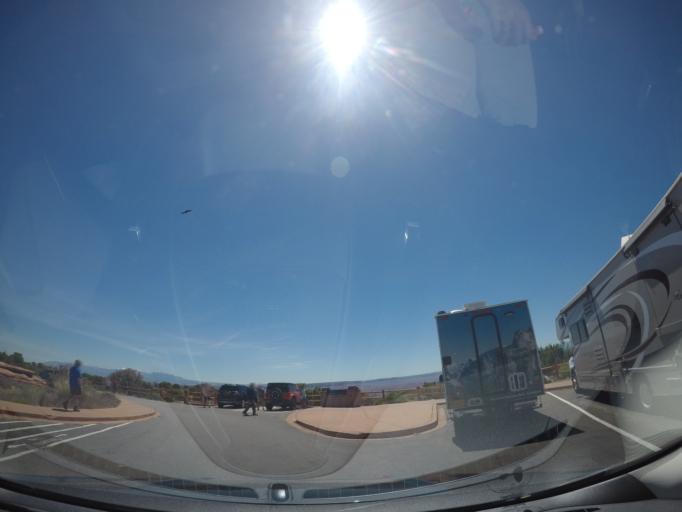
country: US
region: Utah
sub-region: Grand County
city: Moab
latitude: 38.3109
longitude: -109.8568
